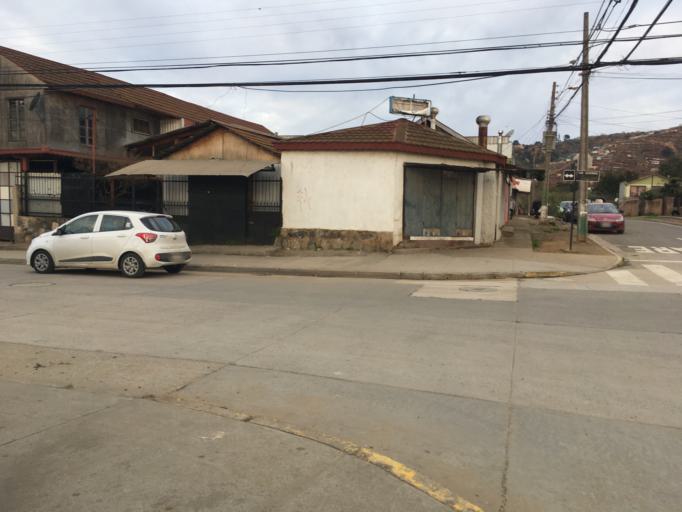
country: CL
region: Valparaiso
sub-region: Provincia de Valparaiso
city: Vina del Mar
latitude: -33.0058
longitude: -71.4964
